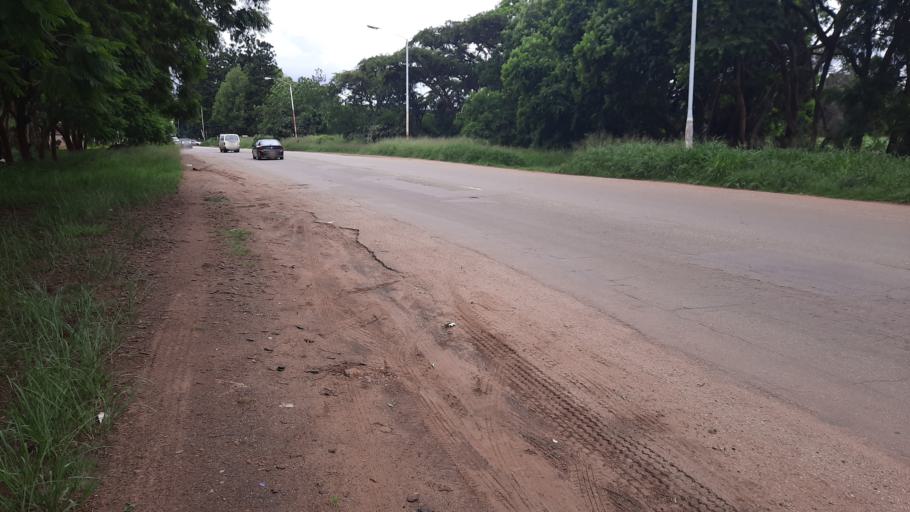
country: ZW
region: Harare
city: Harare
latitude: -17.8204
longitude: 31.0285
